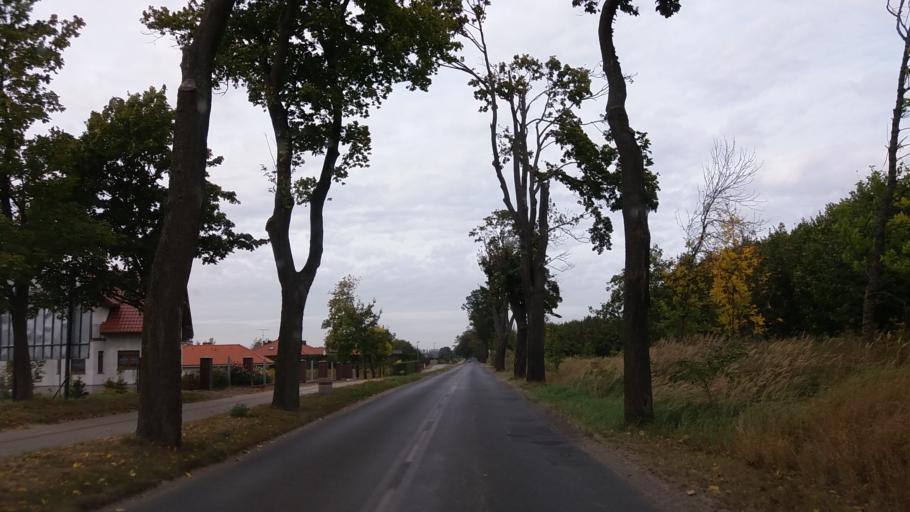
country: PL
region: Lubusz
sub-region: Powiat strzelecko-drezdenecki
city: Strzelce Krajenskie
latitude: 52.8834
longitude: 15.5202
